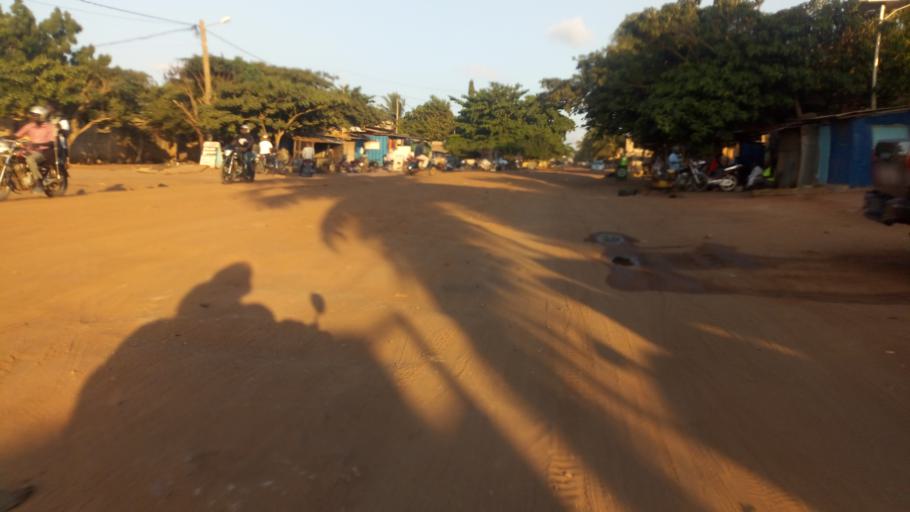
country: TG
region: Maritime
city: Lome
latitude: 6.2207
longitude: 1.1819
